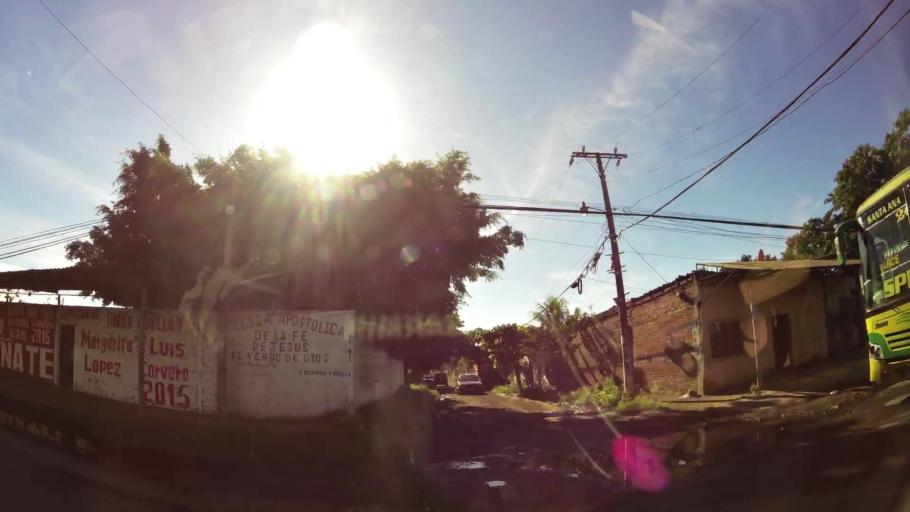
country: SV
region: Santa Ana
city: Santa Ana
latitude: 13.9768
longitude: -89.5818
